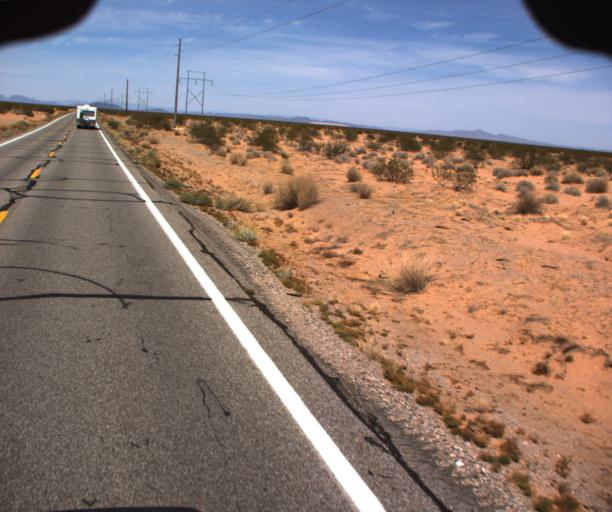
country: US
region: Arizona
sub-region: La Paz County
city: Quartzsite
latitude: 33.8935
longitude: -114.2169
